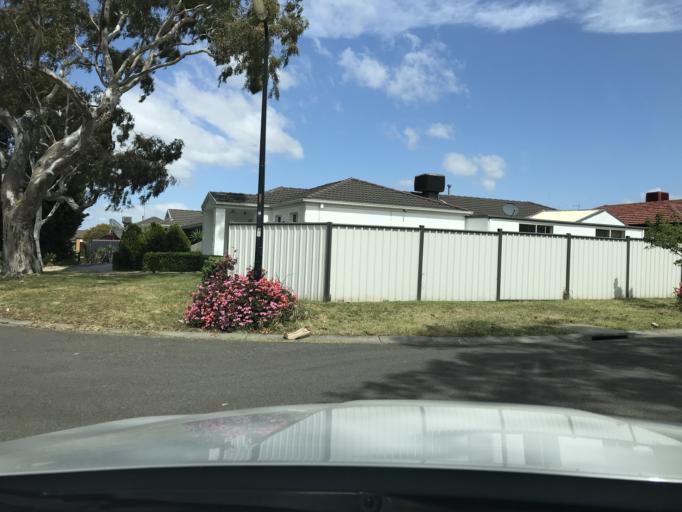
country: AU
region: Victoria
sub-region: Hume
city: Roxburgh Park
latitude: -37.6155
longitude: 144.9390
